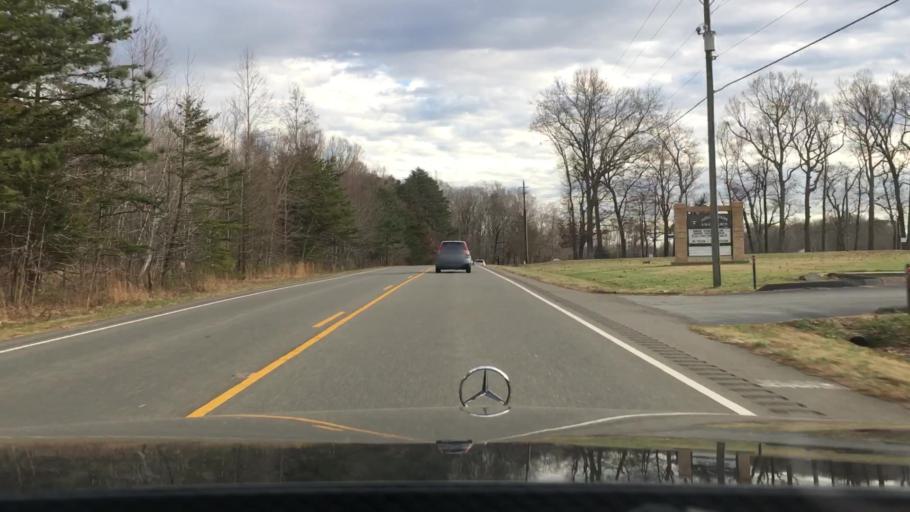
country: US
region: North Carolina
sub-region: Orange County
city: Hillsborough
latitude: 36.1701
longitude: -79.1318
